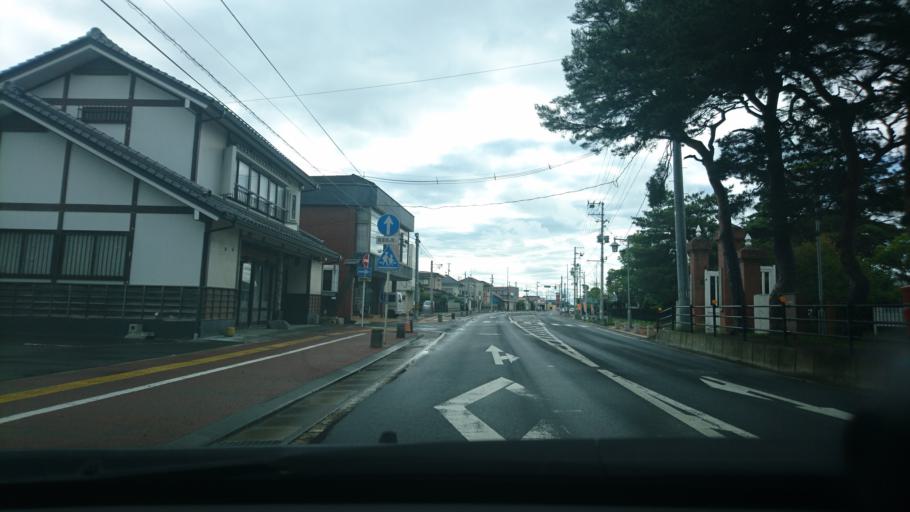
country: JP
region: Miyagi
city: Wakuya
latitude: 38.6547
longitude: 141.2802
